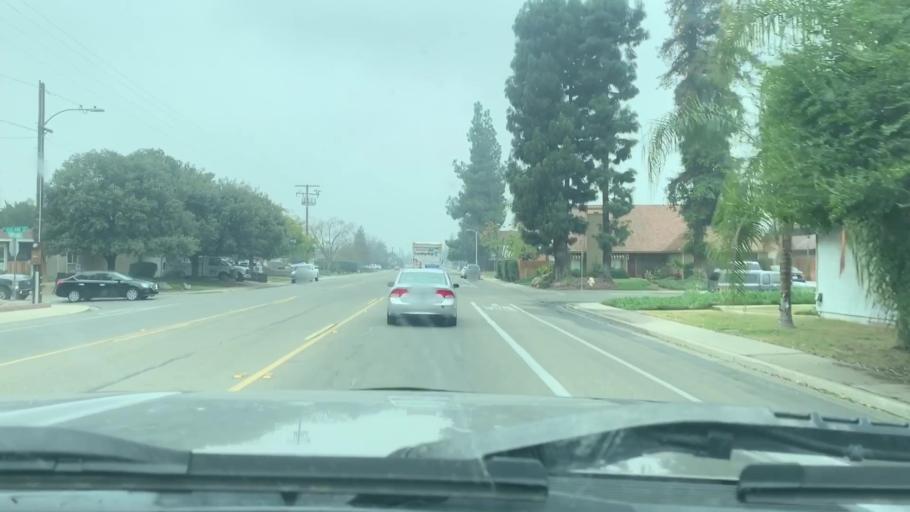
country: US
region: California
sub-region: Tulare County
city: Visalia
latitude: 36.3089
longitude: -119.3228
